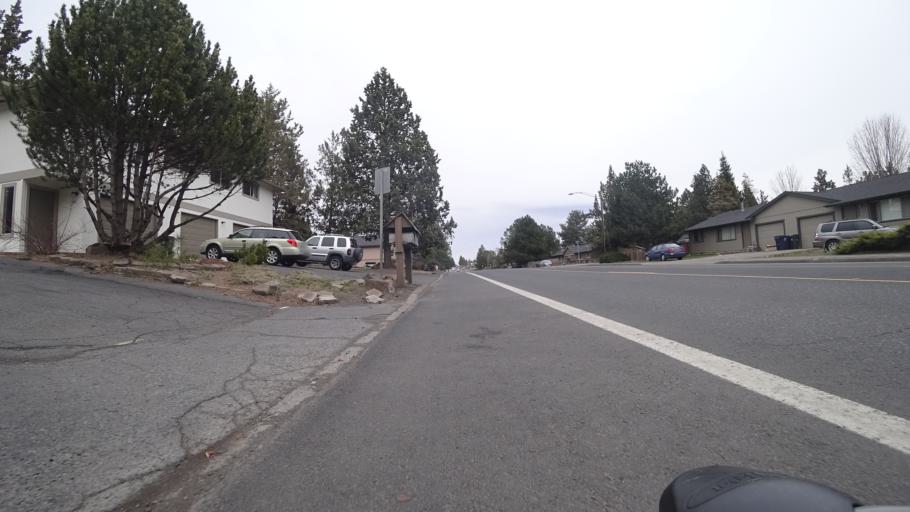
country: US
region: Oregon
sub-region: Deschutes County
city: Bend
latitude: 44.0444
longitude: -121.2974
